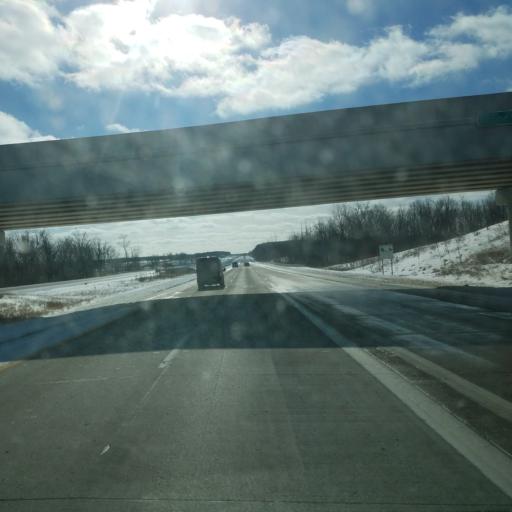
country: US
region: Michigan
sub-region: Clinton County
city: DeWitt
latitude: 42.8568
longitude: -84.5190
